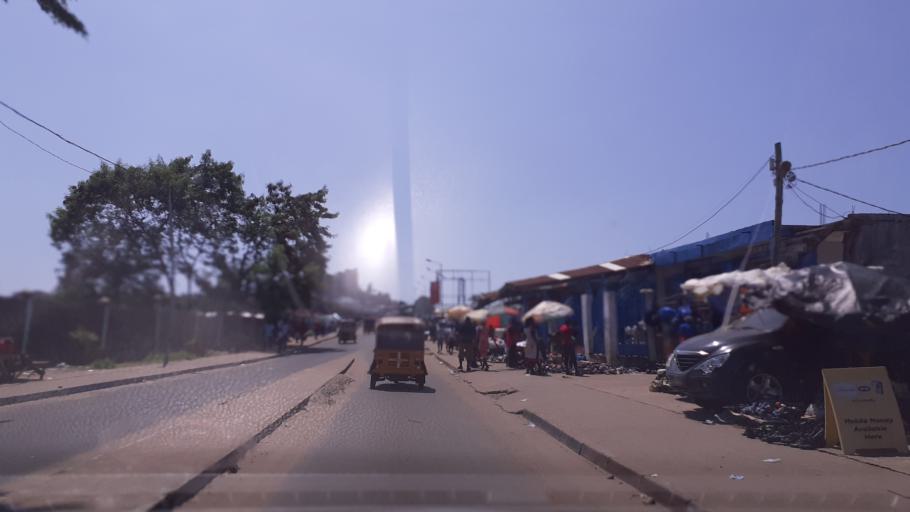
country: LR
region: Montserrado
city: Monrovia
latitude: 6.3228
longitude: -10.8034
